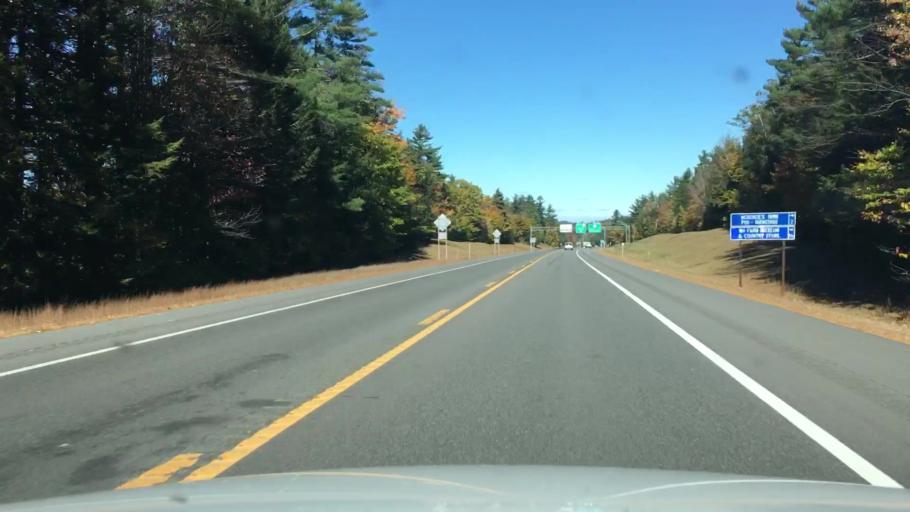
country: US
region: New Hampshire
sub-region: Carroll County
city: Sanbornville
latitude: 43.4729
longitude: -71.0015
